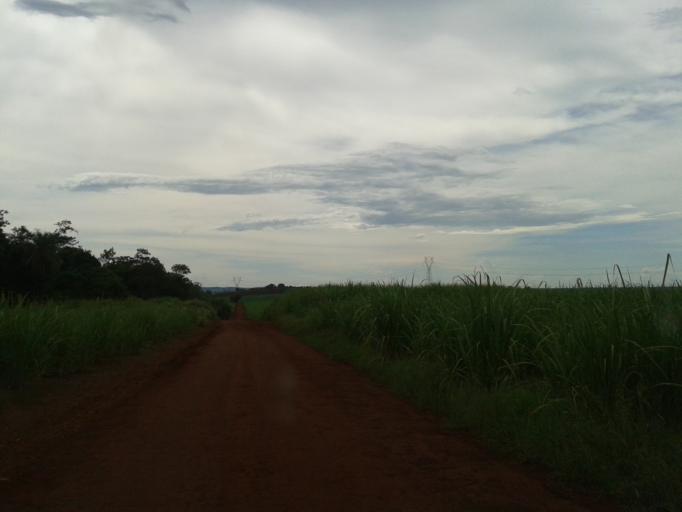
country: BR
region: Minas Gerais
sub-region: Centralina
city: Centralina
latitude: -18.6462
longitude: -49.3246
